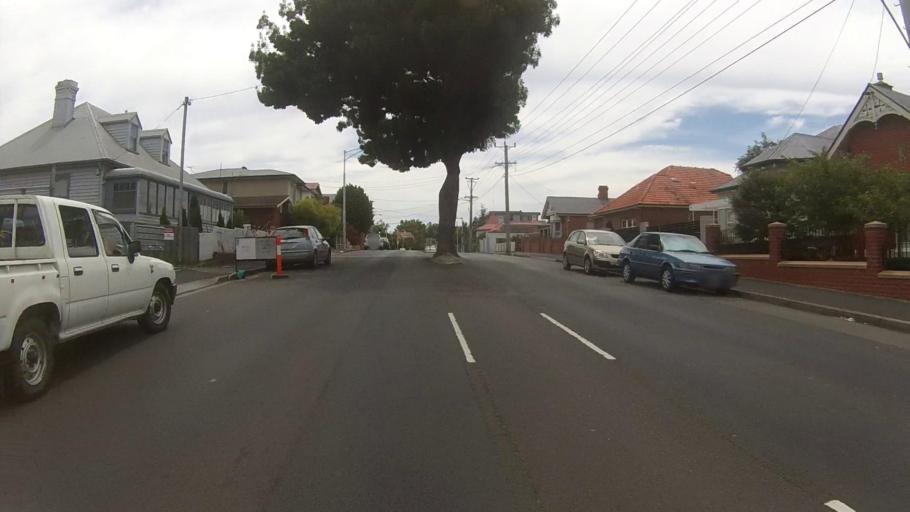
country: AU
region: Tasmania
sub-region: Hobart
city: Sandy Bay
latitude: -42.8964
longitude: 147.3235
